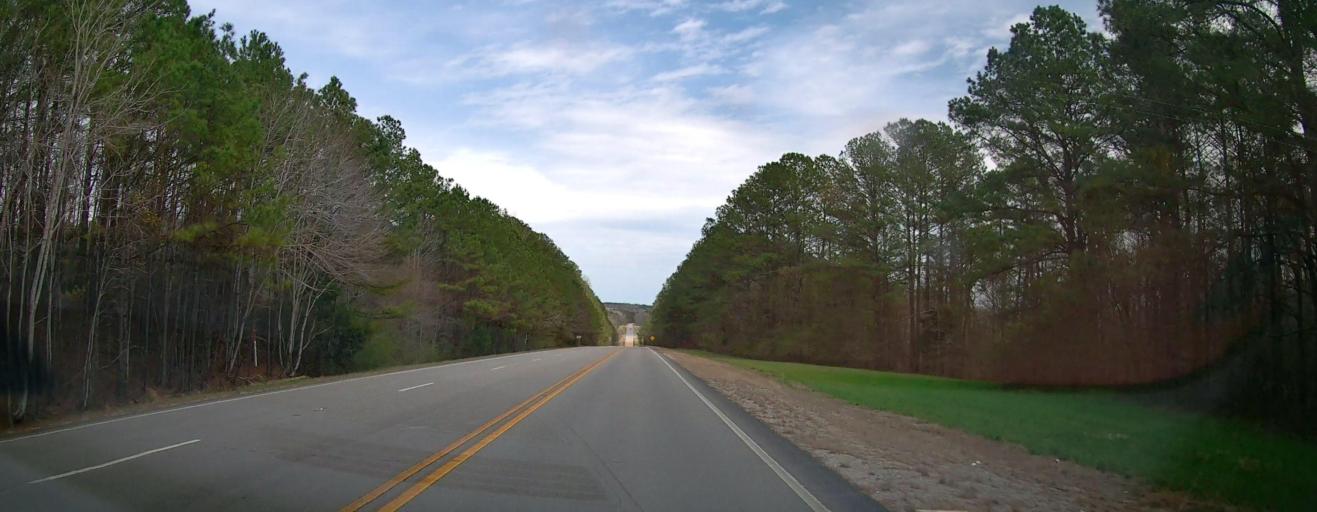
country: US
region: Alabama
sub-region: Marion County
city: Winfield
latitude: 33.9317
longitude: -87.7444
